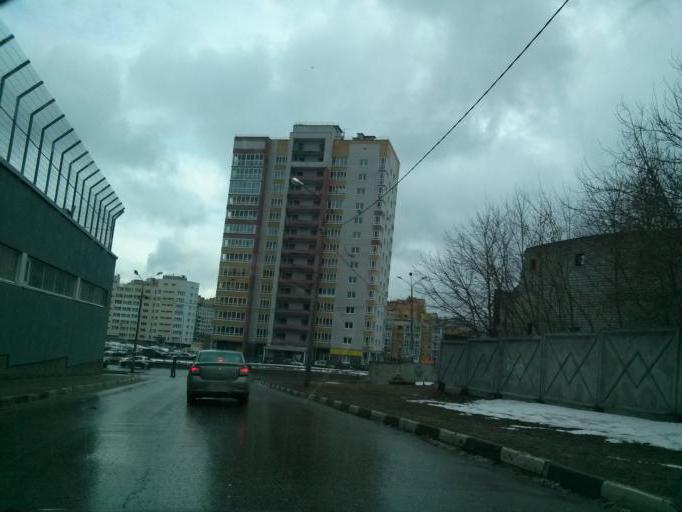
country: RU
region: Nizjnij Novgorod
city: Afonino
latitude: 56.3062
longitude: 44.0731
